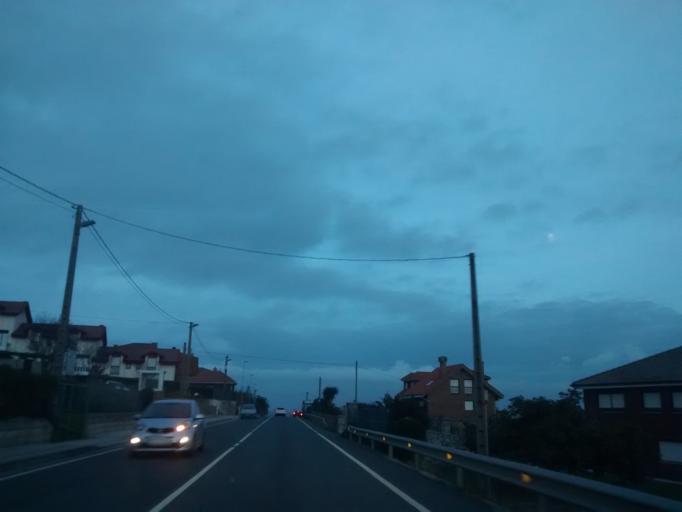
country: ES
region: Cantabria
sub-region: Provincia de Cantabria
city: Santa Cruz de Bezana
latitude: 43.4610
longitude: -3.9242
